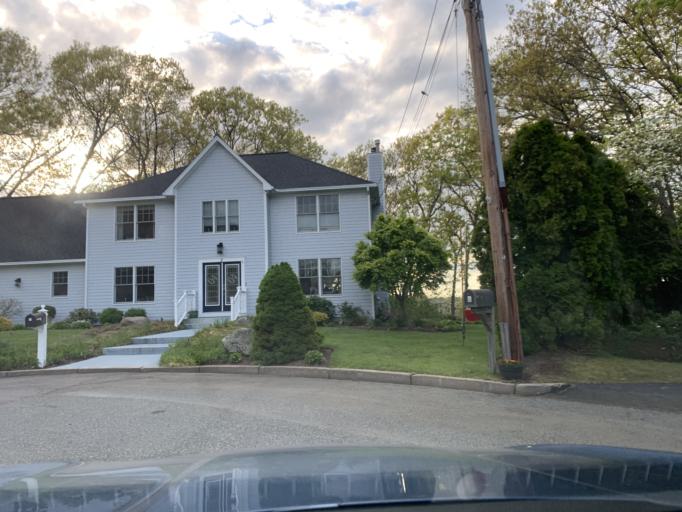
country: US
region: Rhode Island
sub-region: Kent County
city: East Greenwich
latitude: 41.6466
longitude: -71.4498
